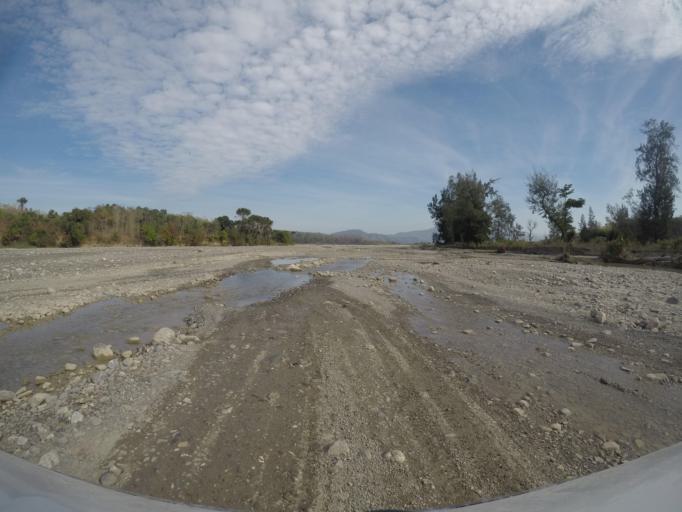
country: TL
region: Bobonaro
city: Maliana
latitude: -8.9044
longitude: 125.2100
